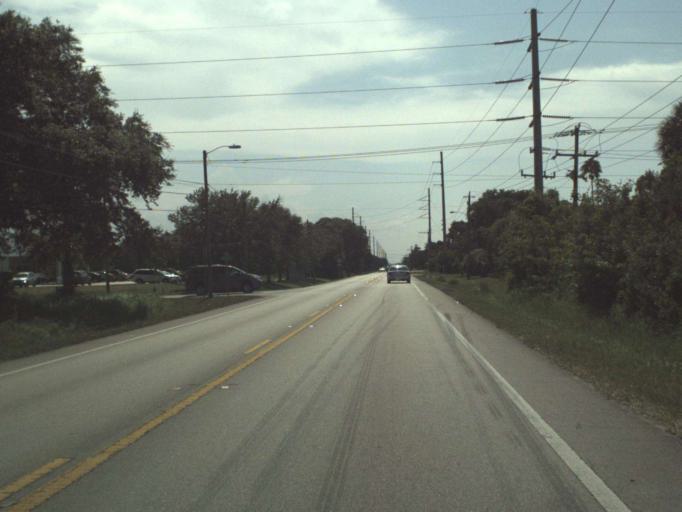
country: US
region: Florida
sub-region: Brevard County
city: Palm Bay
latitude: 27.9983
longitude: -80.6051
